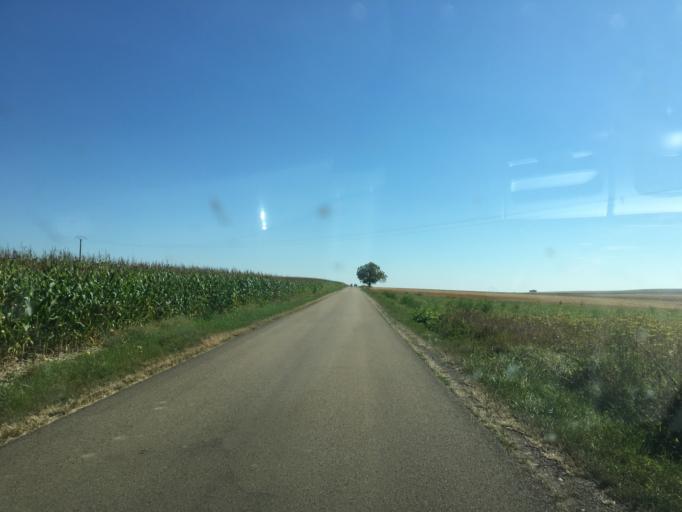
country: FR
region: Bourgogne
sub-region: Departement de l'Yonne
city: Aillant-sur-Tholon
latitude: 47.9124
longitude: 3.3629
